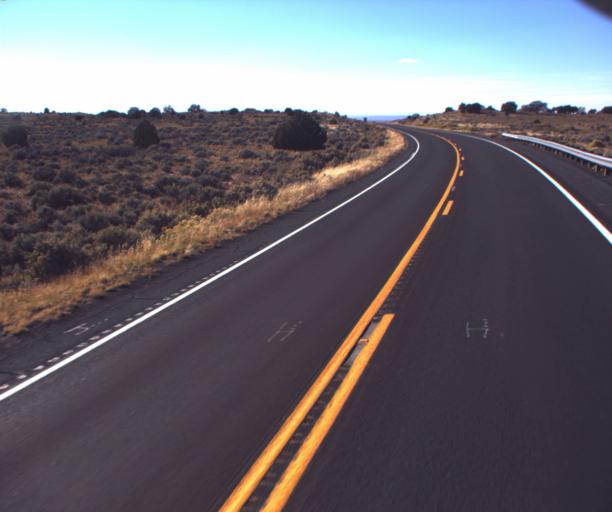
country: US
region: Arizona
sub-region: Coconino County
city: Kaibito
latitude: 36.6139
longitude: -110.9257
